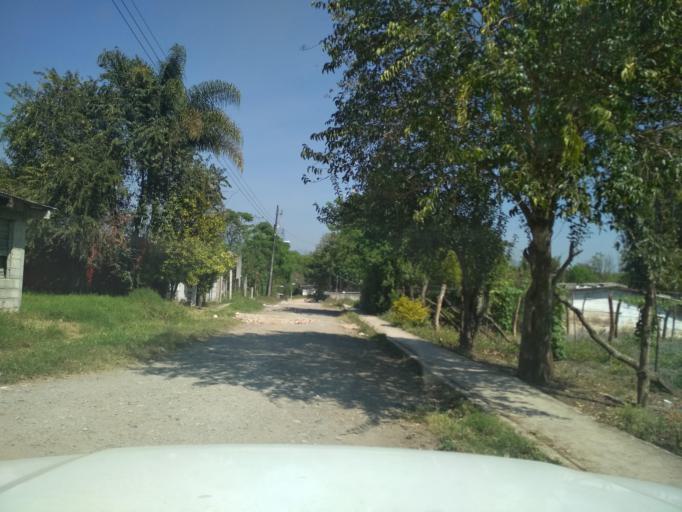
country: MX
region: Veracruz
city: Jalapilla
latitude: 18.8160
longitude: -97.0851
